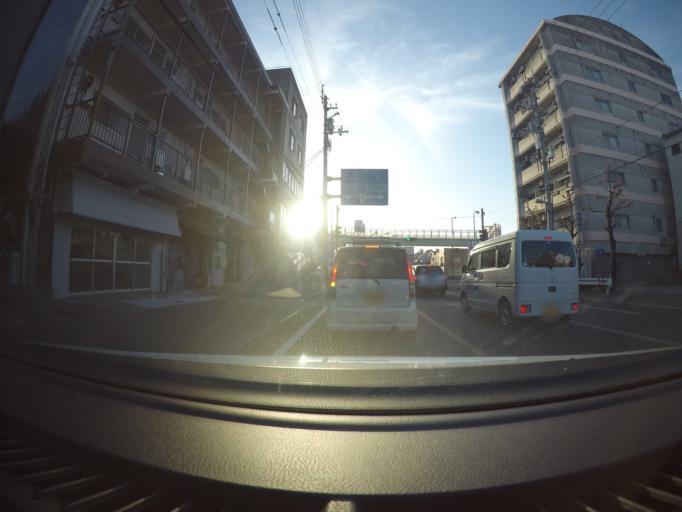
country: JP
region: Kochi
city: Kochi-shi
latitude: 33.5566
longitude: 133.5552
